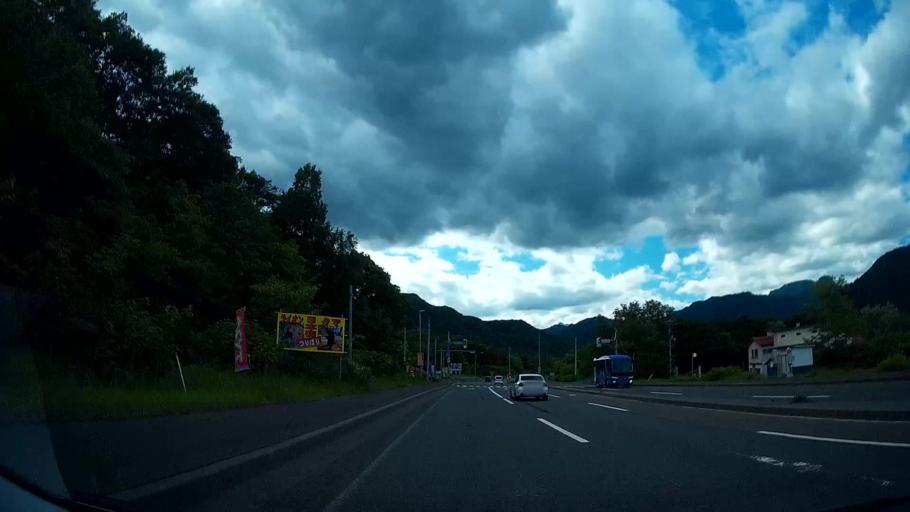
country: JP
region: Hokkaido
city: Sapporo
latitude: 42.9574
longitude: 141.2313
